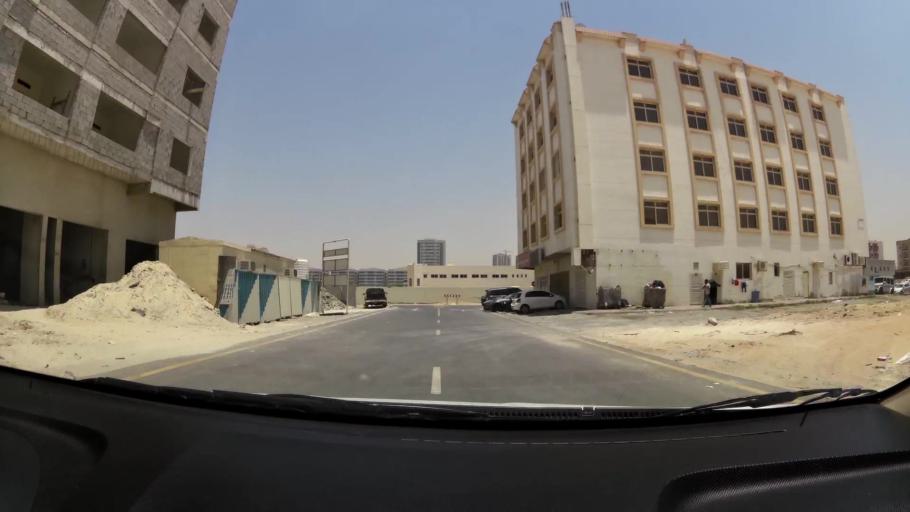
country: AE
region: Ajman
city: Ajman
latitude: 25.4041
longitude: 55.5018
